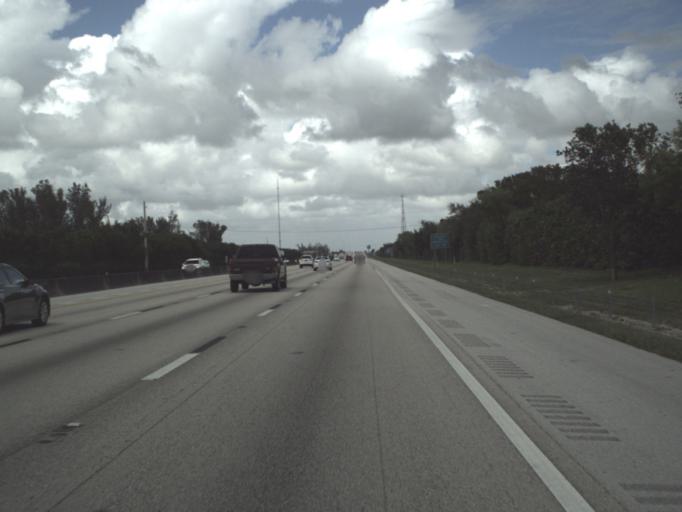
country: US
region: Florida
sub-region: Palm Beach County
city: Boca Pointe
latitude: 26.3541
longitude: -80.1705
